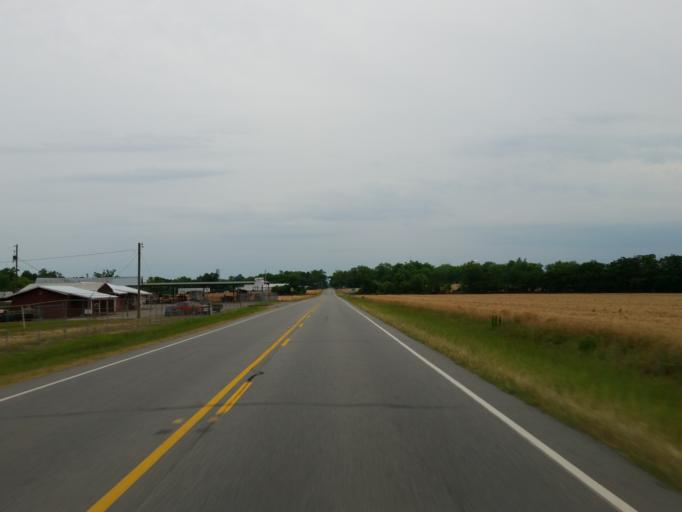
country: US
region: Georgia
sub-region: Dooly County
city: Unadilla
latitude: 32.2047
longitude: -83.7602
